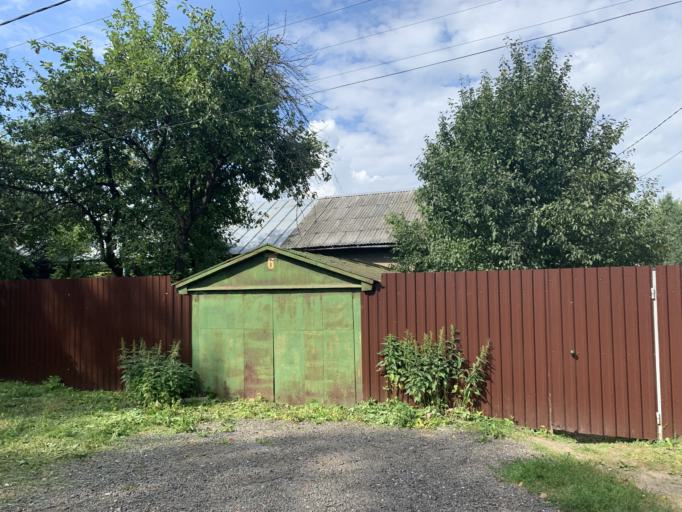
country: RU
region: Moskovskaya
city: Mamontovka
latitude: 55.9853
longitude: 37.8089
